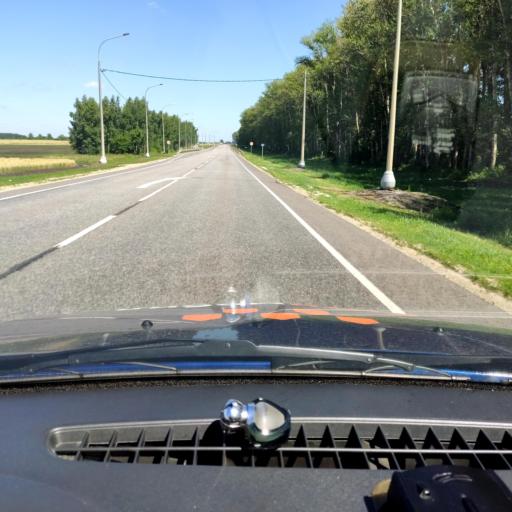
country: RU
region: Orjol
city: Pokrovskoye
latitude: 52.6196
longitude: 36.7482
